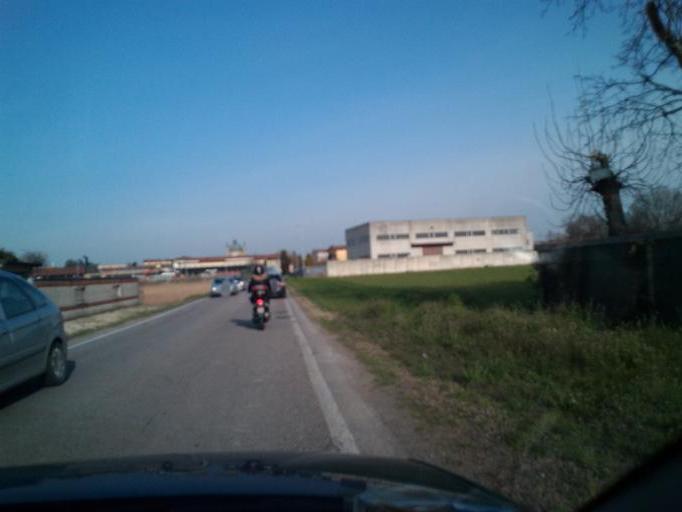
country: IT
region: Veneto
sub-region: Provincia di Verona
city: Villafranca di Verona
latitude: 45.3482
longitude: 10.8515
